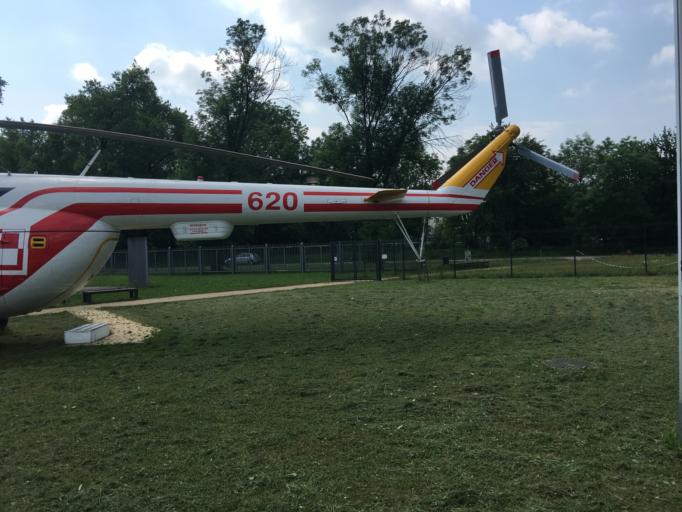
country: PL
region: Lesser Poland Voivodeship
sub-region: Krakow
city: Krakow
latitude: 50.0770
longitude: 19.9904
